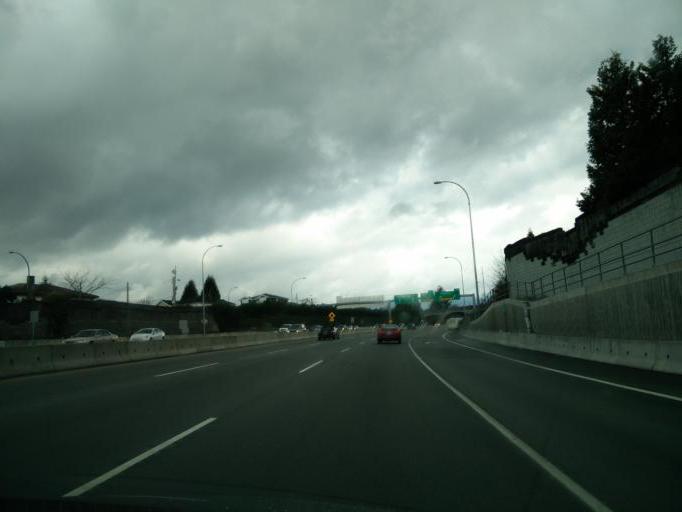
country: CA
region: British Columbia
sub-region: Fraser Valley Regional District
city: North Vancouver
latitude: 49.2746
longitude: -123.0307
